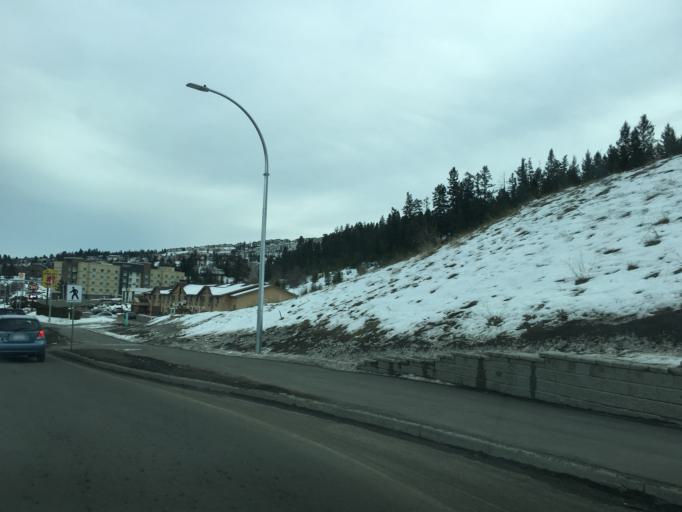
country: CA
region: British Columbia
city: Kamloops
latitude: 50.6529
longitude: -120.3832
